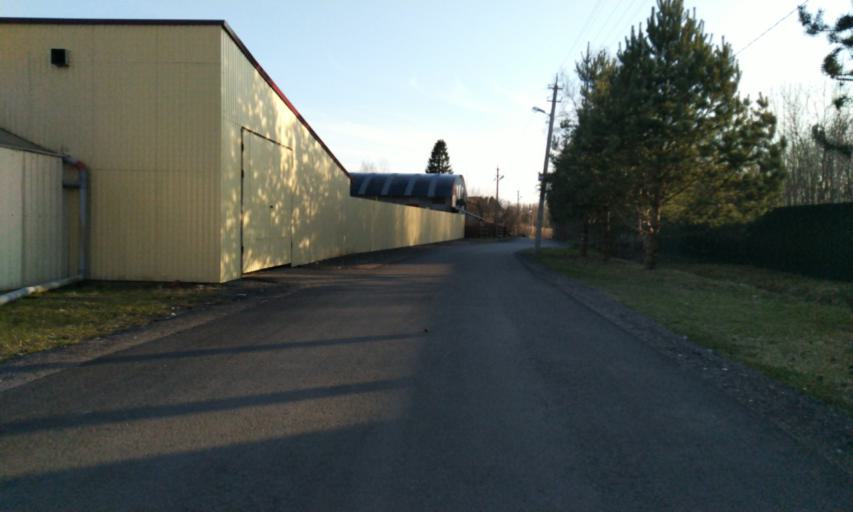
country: RU
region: Leningrad
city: Novoye Devyatkino
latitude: 60.1079
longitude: 30.4582
